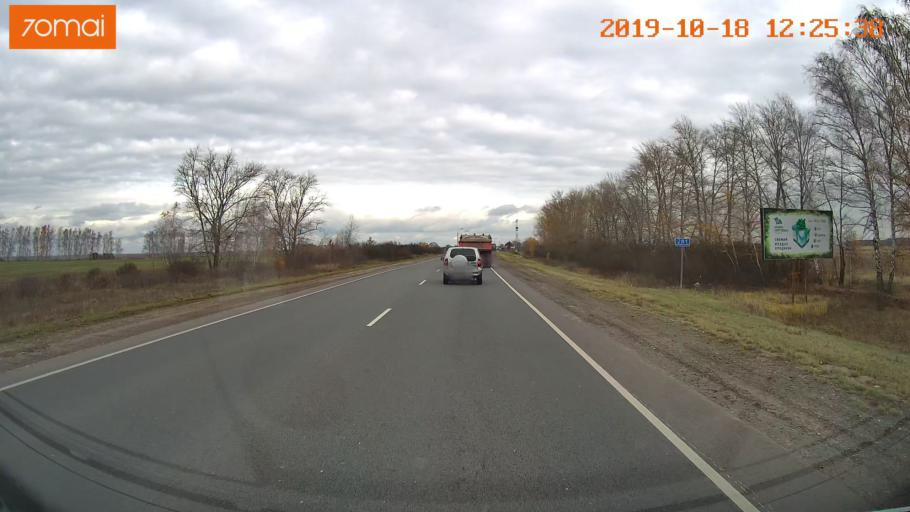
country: RU
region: Rjazan
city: Rybnoye
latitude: 54.5518
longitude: 39.5229
